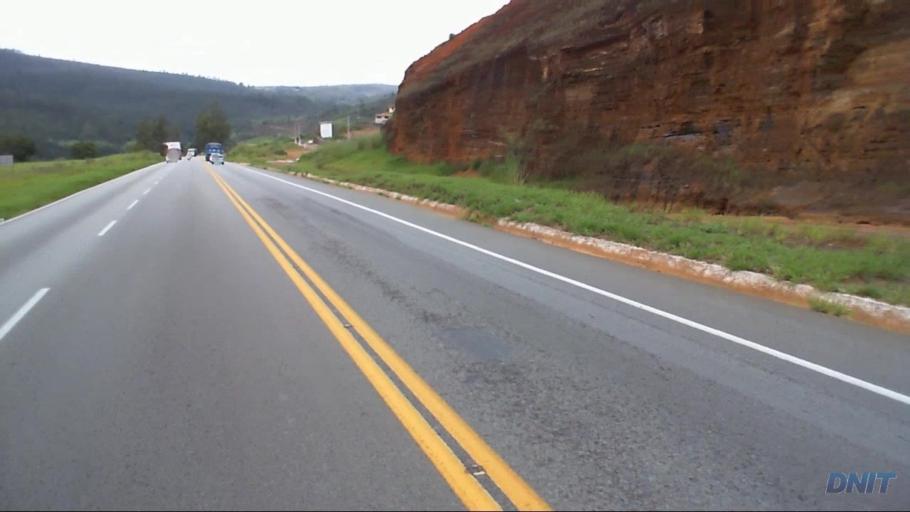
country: BR
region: Minas Gerais
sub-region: Joao Monlevade
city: Joao Monlevade
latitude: -19.8310
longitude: -43.0947
